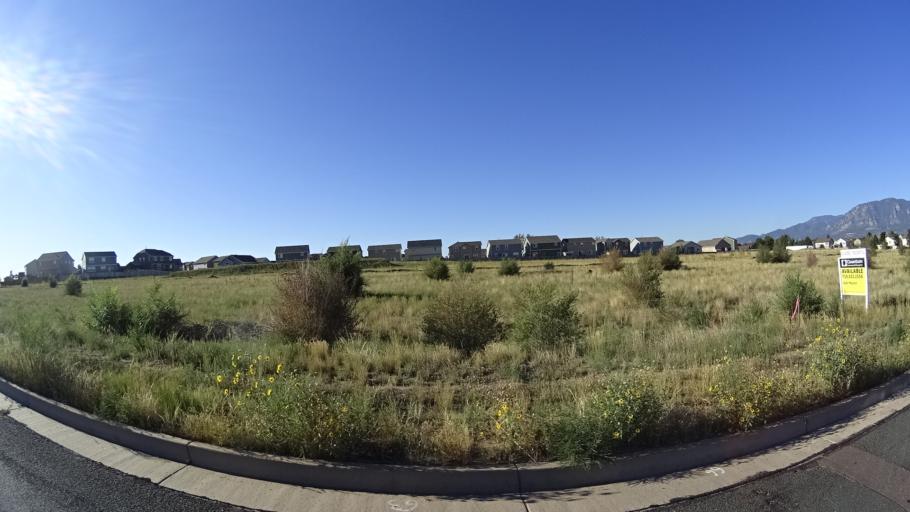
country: US
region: Colorado
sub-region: El Paso County
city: Security-Widefield
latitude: 38.7885
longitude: -104.7319
